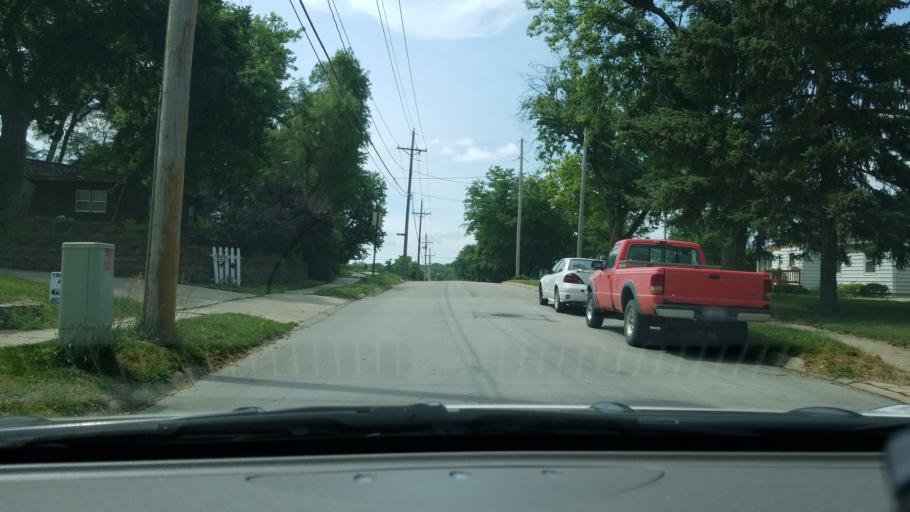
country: US
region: Nebraska
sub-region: Sarpy County
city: Papillion
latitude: 41.1610
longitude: -96.0442
